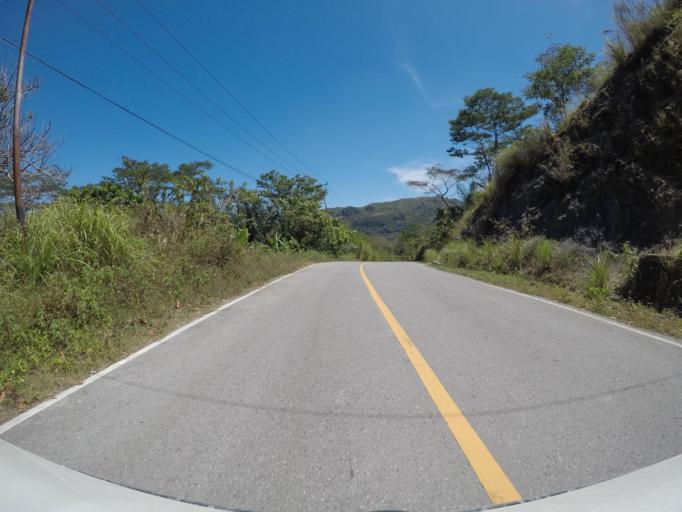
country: TL
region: Manatuto
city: Manatuto
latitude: -8.7823
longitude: 125.9679
